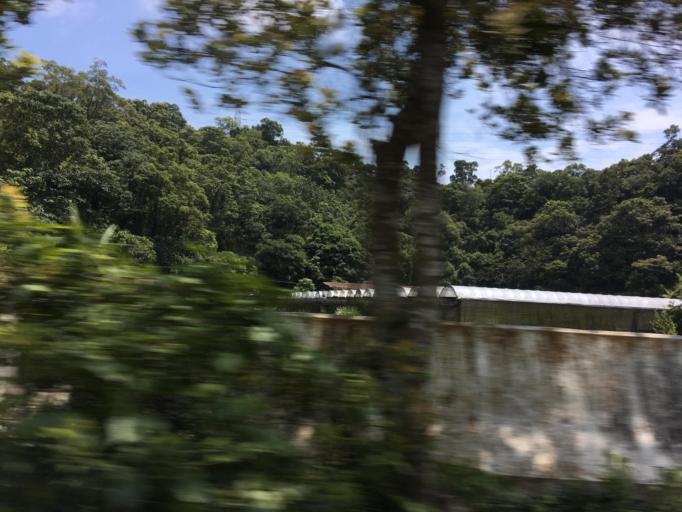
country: TW
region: Taiwan
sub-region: Yilan
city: Yilan
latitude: 24.8170
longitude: 121.7459
